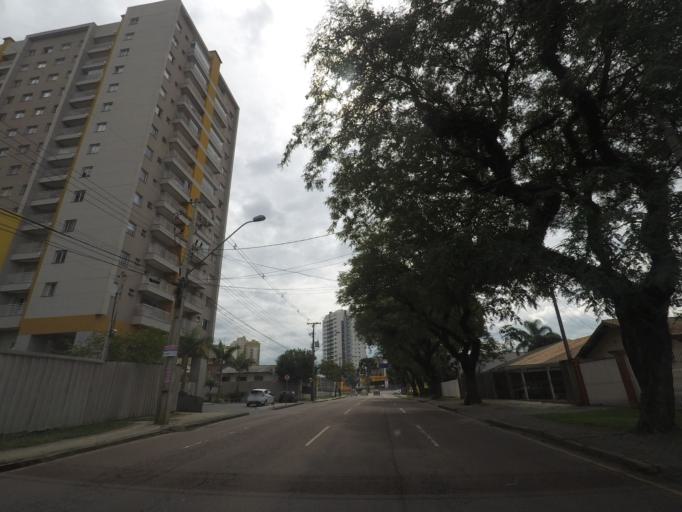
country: BR
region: Parana
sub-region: Curitiba
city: Curitiba
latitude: -25.4989
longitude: -49.2947
